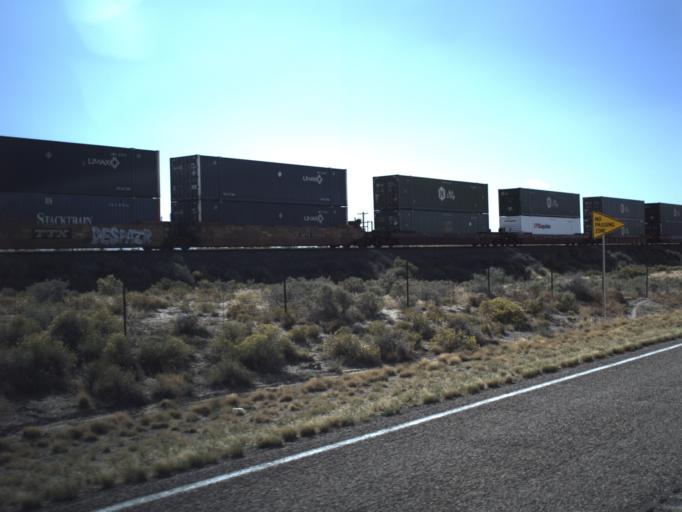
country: US
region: Utah
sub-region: Beaver County
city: Milford
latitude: 38.6774
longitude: -112.9790
